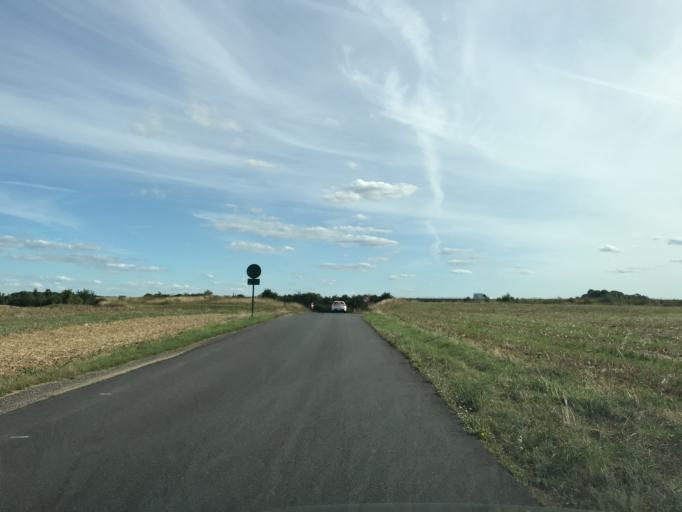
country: FR
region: Ile-de-France
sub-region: Departement du Val-d'Oise
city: Magny-en-Vexin
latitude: 49.1444
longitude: 1.8090
